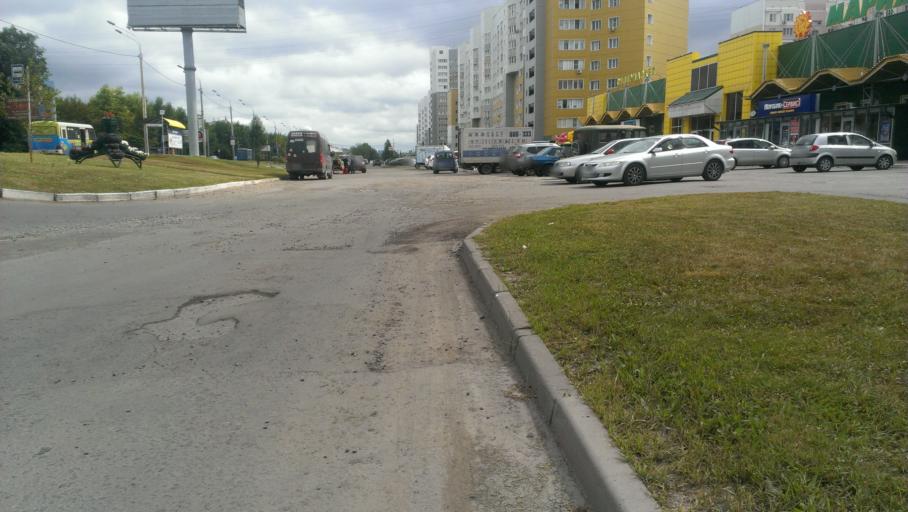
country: RU
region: Altai Krai
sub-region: Gorod Barnaulskiy
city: Barnaul
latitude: 53.3411
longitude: 83.7047
